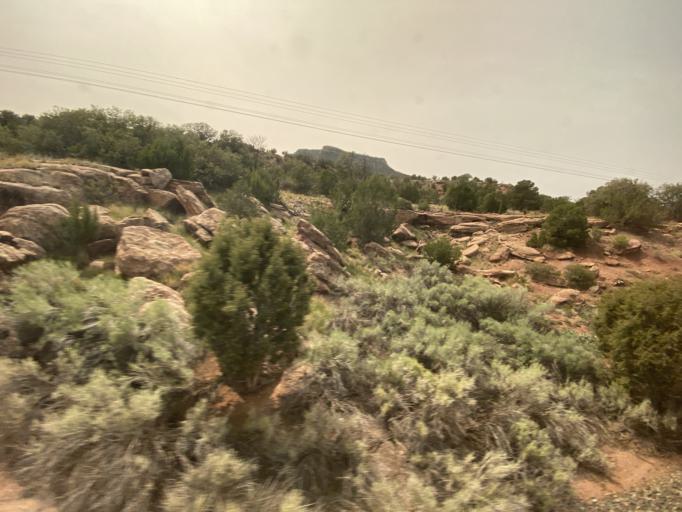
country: US
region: New Mexico
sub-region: San Miguel County
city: Pecos
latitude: 35.4011
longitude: -105.4953
